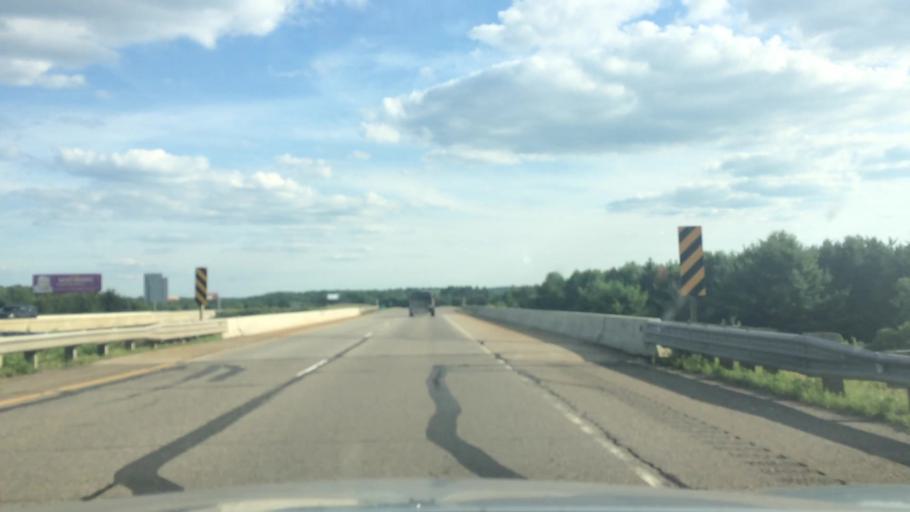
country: US
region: Wisconsin
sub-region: Lincoln County
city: Merrill
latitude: 45.1583
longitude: -89.6440
